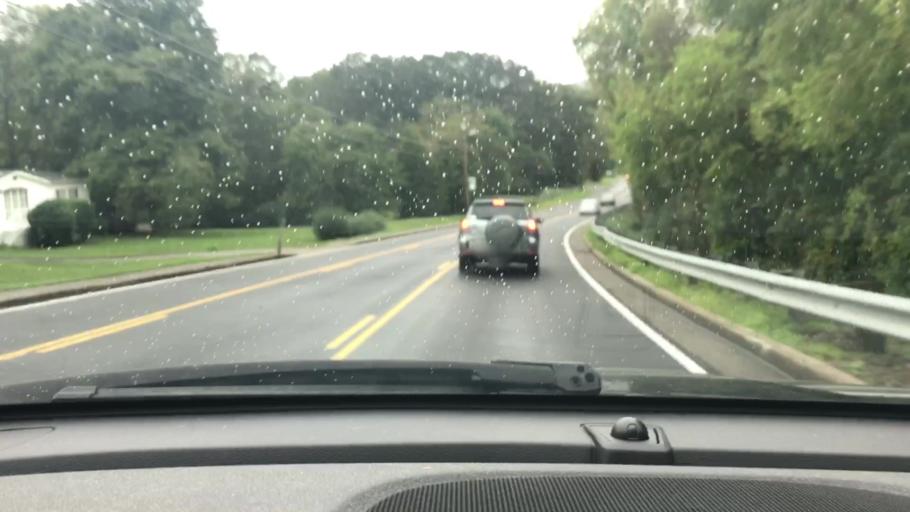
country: US
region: Tennessee
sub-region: Cheatham County
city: Kingston Springs
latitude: 36.0879
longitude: -87.1049
